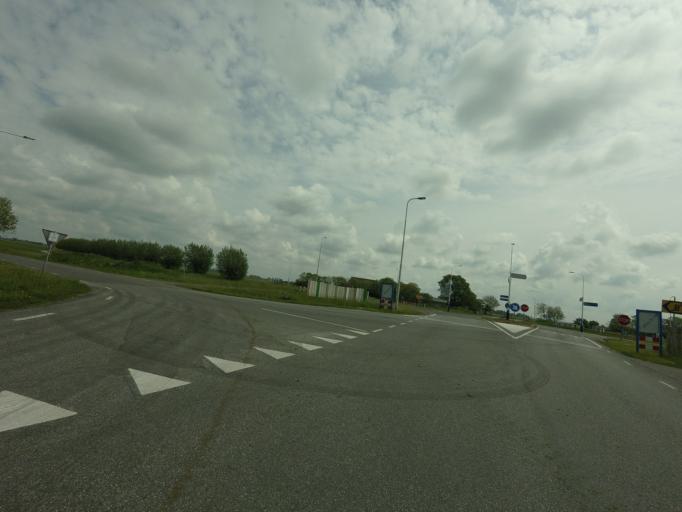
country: NL
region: Friesland
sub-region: Sudwest Fryslan
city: Bolsward
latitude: 53.0937
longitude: 5.5336
